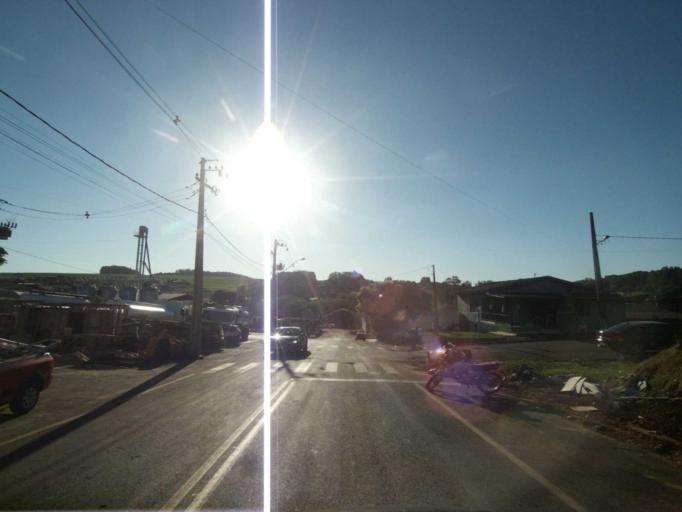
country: BR
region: Parana
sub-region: Coronel Vivida
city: Coronel Vivida
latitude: -25.9777
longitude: -52.8138
